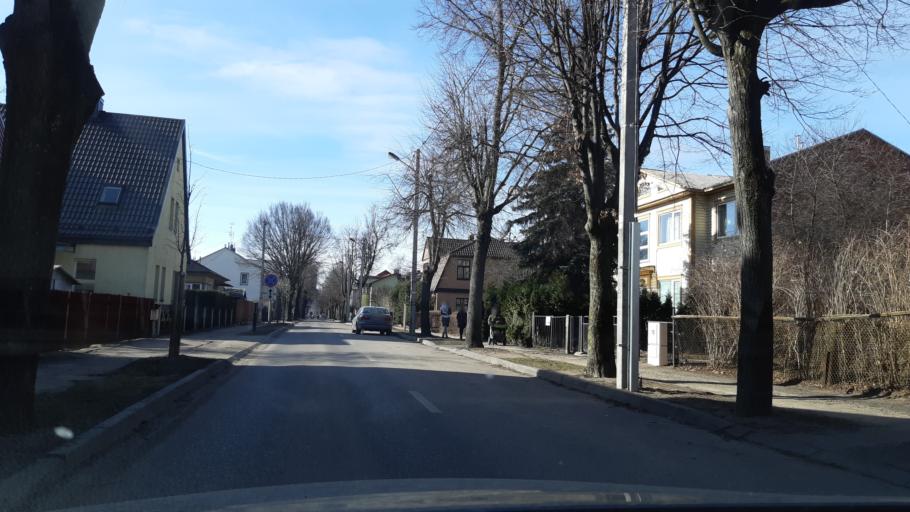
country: LT
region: Kauno apskritis
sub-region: Kaunas
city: Eiguliai
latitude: 54.9072
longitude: 23.9295
